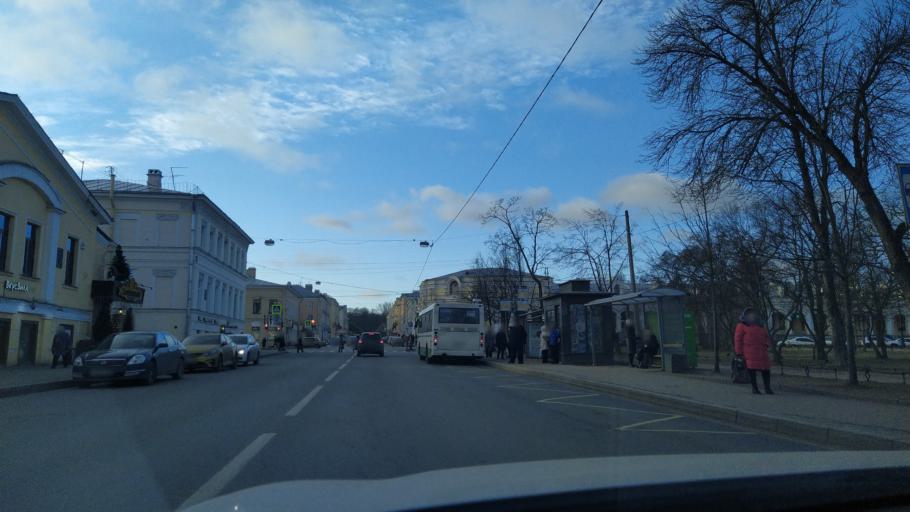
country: RU
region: St.-Petersburg
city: Pushkin
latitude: 59.7198
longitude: 30.4088
